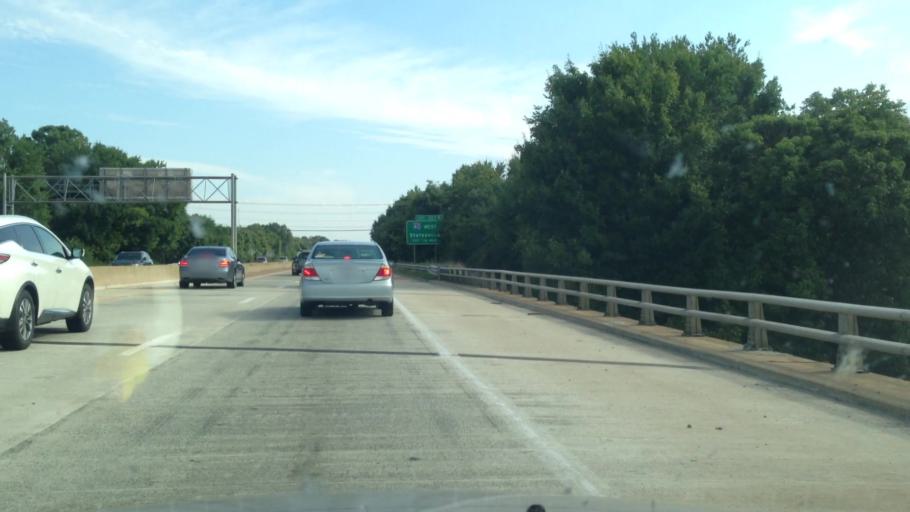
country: US
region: North Carolina
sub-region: Forsyth County
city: Winston-Salem
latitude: 36.0704
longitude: -80.2286
